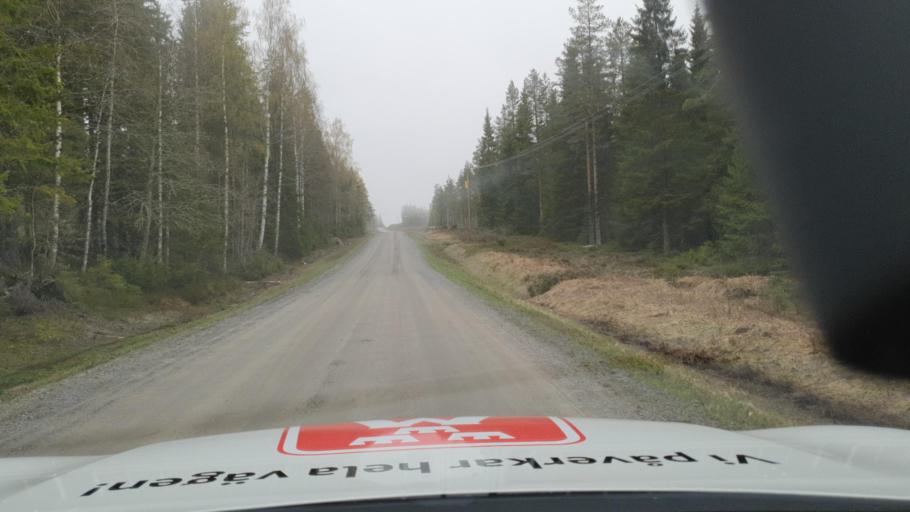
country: SE
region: Vaesterbotten
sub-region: Nordmalings Kommun
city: Nordmaling
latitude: 63.7460
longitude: 19.5006
